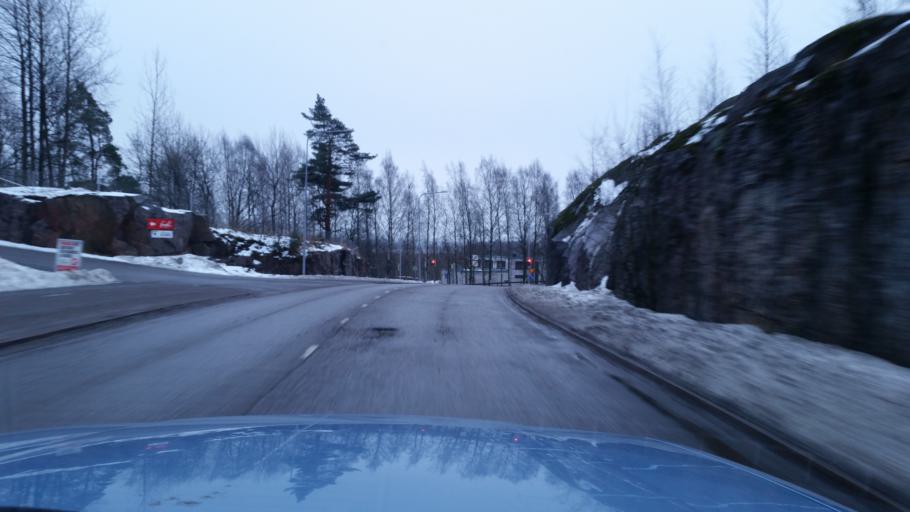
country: FI
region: Uusimaa
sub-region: Helsinki
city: Helsinki
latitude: 60.2223
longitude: 24.9899
